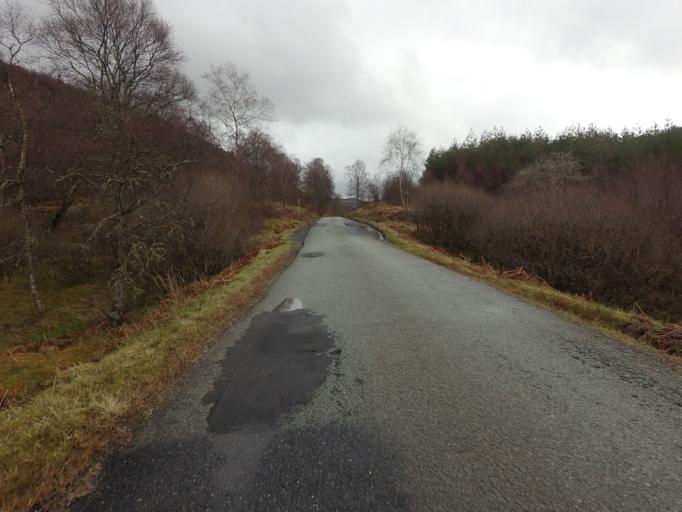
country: GB
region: Scotland
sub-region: West Dunbartonshire
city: Balloch
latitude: 56.2433
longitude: -4.5731
